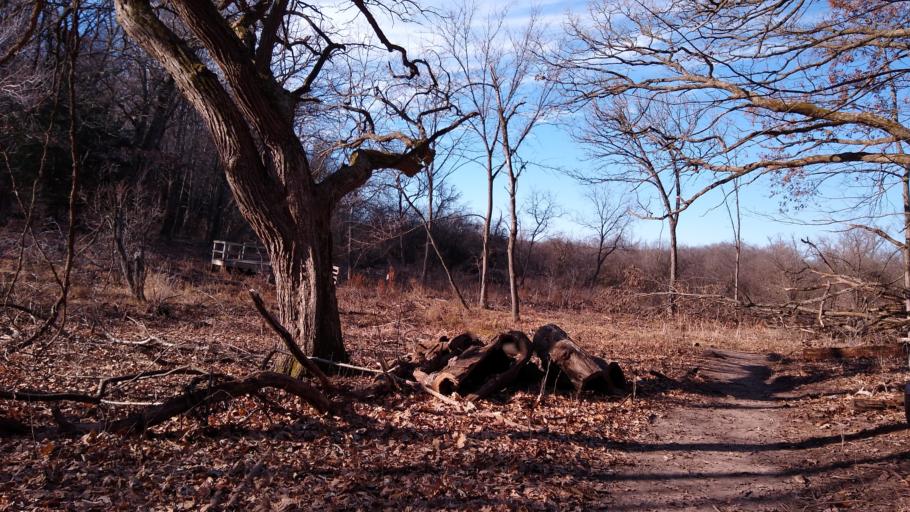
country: US
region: Wisconsin
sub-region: Dane County
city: Madison
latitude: 43.0478
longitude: -89.4219
